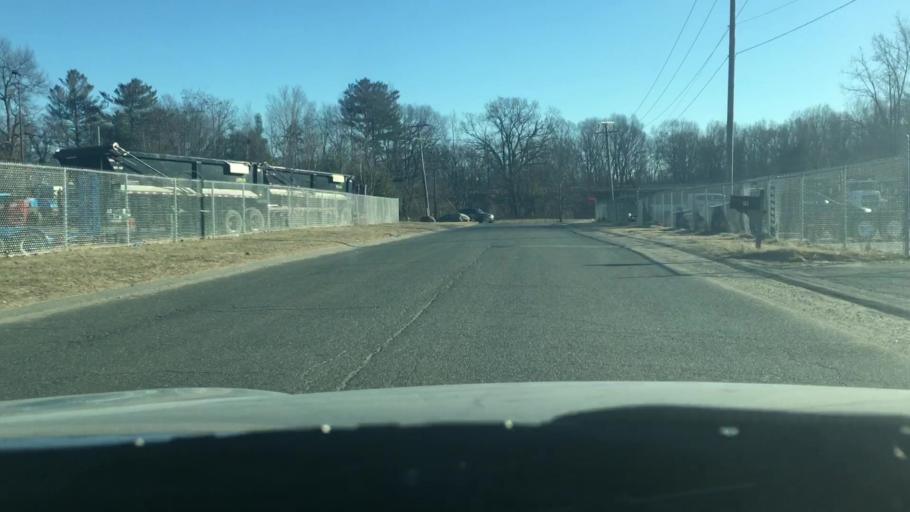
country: US
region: Massachusetts
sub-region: Hampden County
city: Ludlow
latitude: 42.1719
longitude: -72.4460
